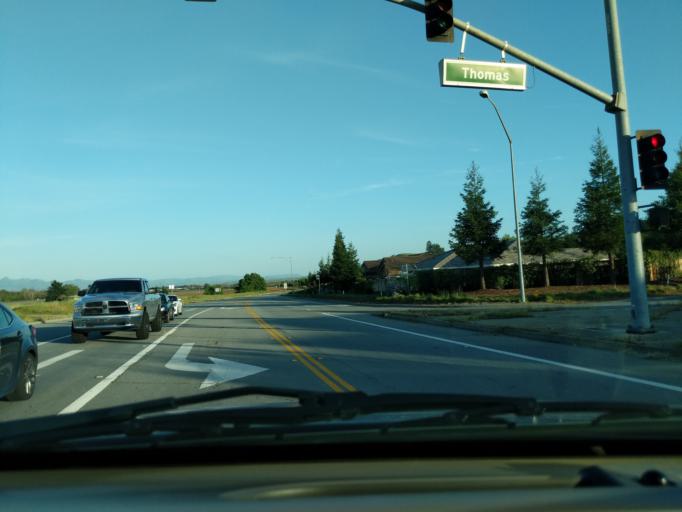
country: US
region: California
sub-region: Santa Clara County
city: Gilroy
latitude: 36.9828
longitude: -121.5733
